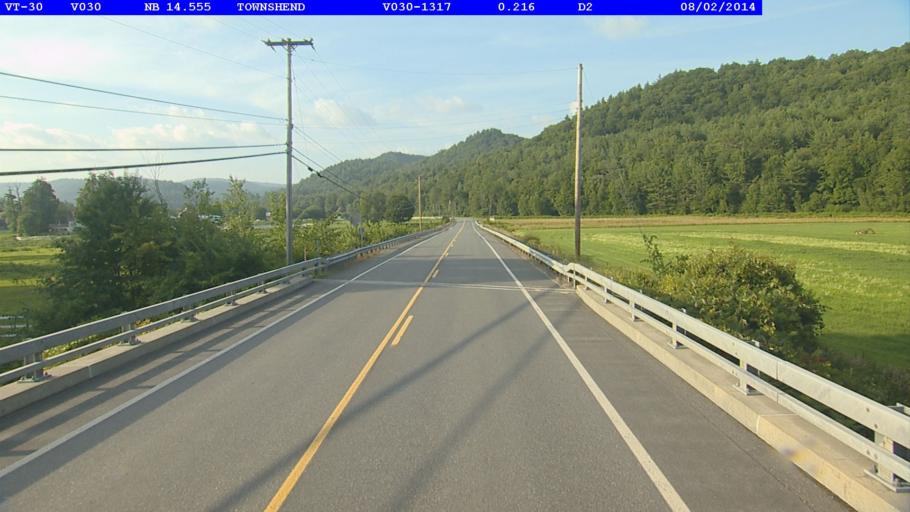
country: US
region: Vermont
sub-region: Windham County
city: Newfane
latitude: 43.0225
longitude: -72.6571
